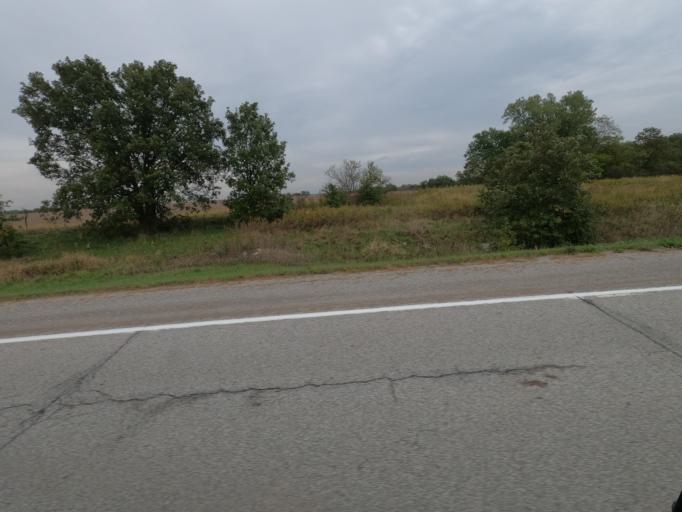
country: US
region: Iowa
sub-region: Van Buren County
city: Keosauqua
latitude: 40.8416
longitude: -92.0111
